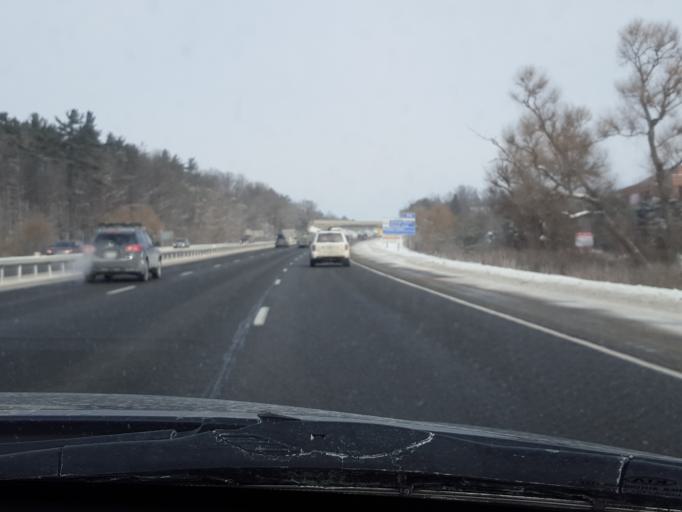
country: CA
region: Ontario
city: Barrie
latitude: 44.3890
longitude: -79.7062
